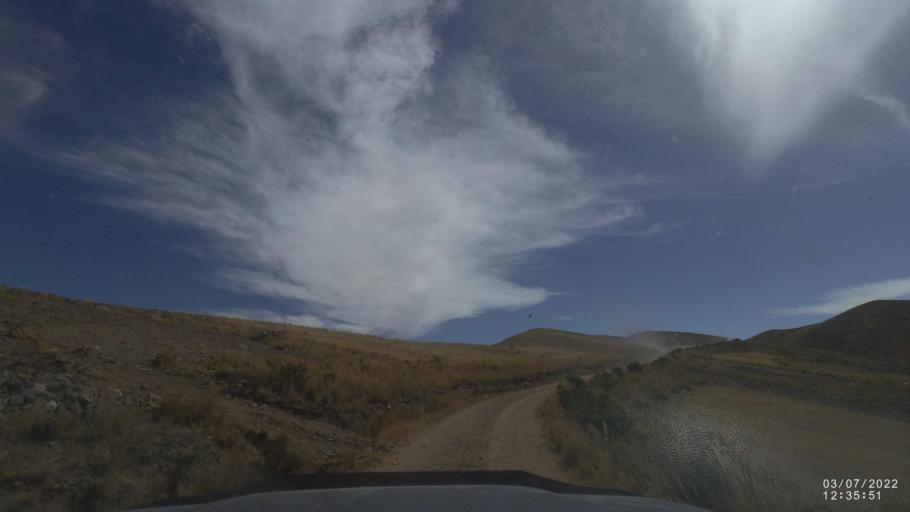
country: BO
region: Cochabamba
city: Irpa Irpa
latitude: -17.8047
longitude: -66.6106
